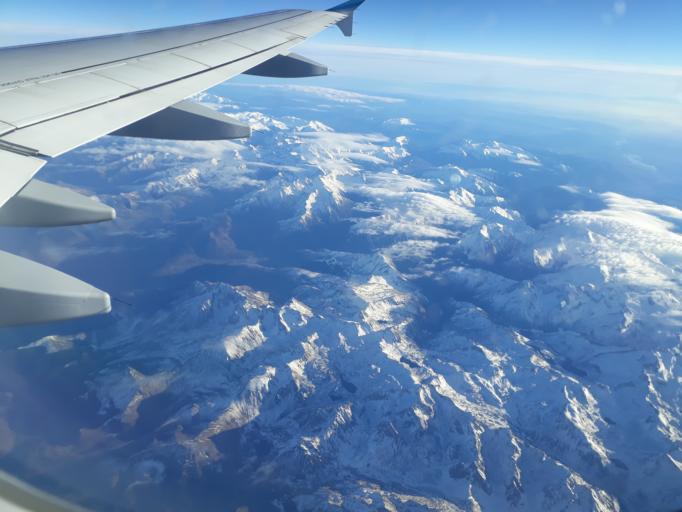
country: FR
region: Midi-Pyrenees
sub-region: Departement des Hautes-Pyrenees
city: Campan
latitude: 42.9918
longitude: 0.1226
